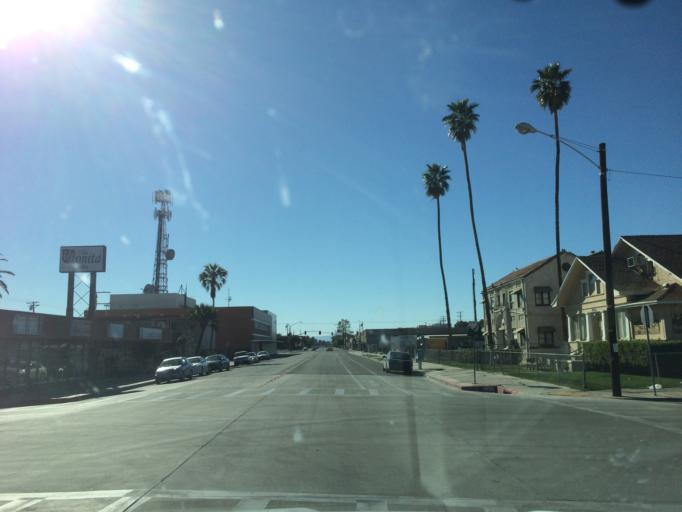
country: US
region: California
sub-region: Imperial County
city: El Centro
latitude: 32.7918
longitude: -115.5589
